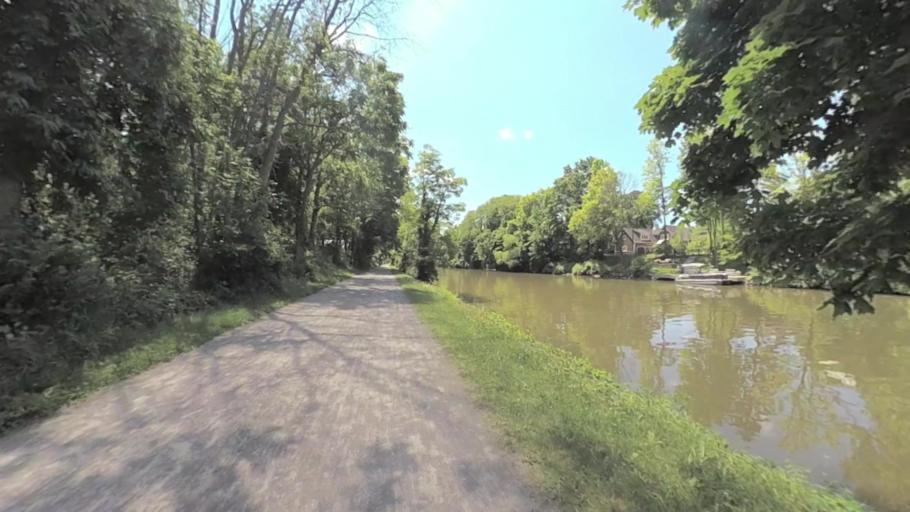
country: US
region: New York
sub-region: Monroe County
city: Pittsford
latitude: 43.0847
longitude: -77.5071
